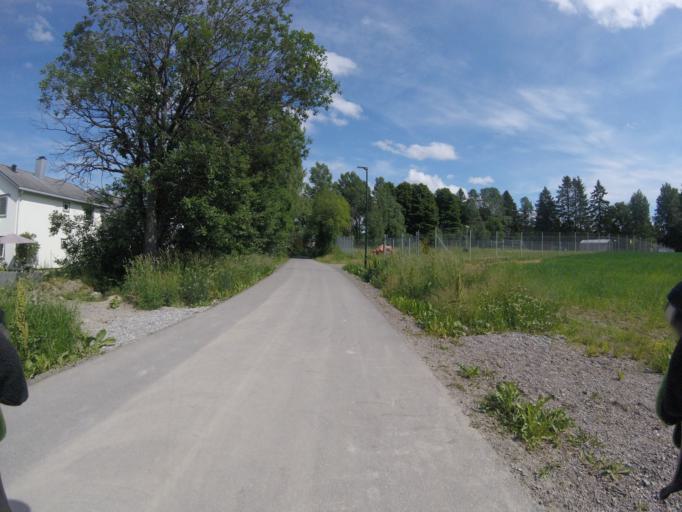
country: NO
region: Akershus
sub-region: Skedsmo
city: Lillestrom
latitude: 59.9807
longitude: 11.0296
